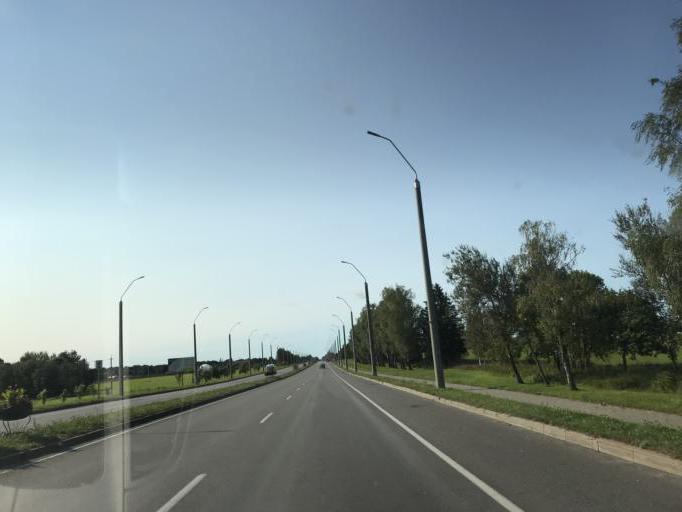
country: BY
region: Mogilev
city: Buynichy
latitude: 53.8706
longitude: 30.2622
